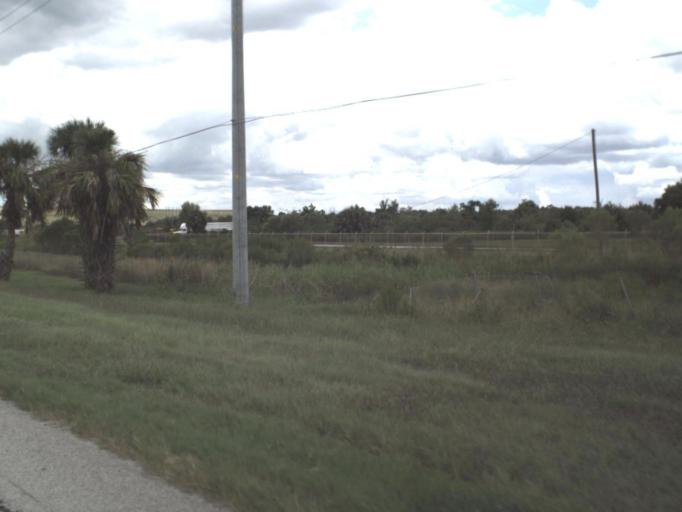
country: US
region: Florida
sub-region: Polk County
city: Bartow
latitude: 27.8982
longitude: -81.8851
